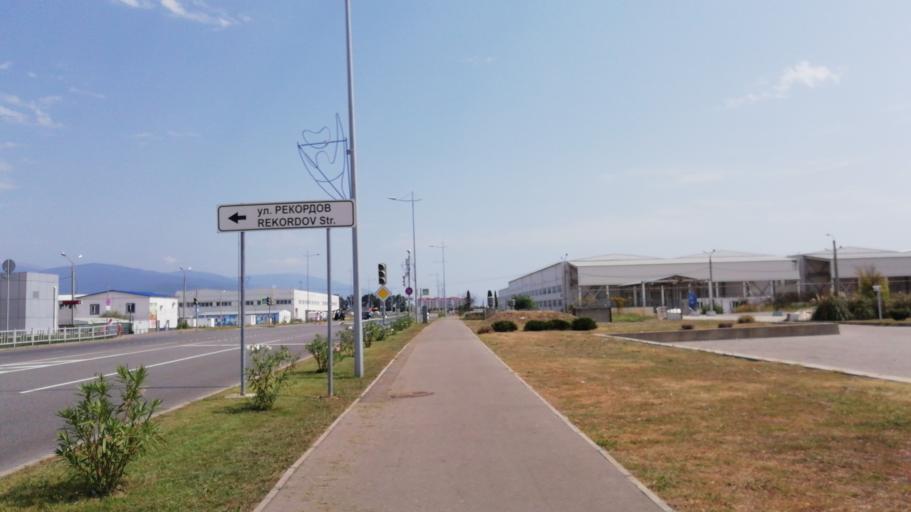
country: RU
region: Krasnodarskiy
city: Adler
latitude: 43.3985
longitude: 39.9825
